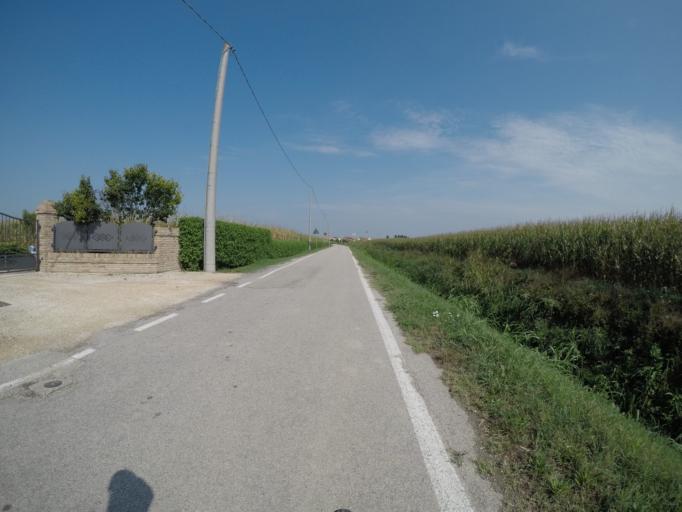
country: IT
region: Veneto
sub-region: Provincia di Rovigo
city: Lendinara
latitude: 45.0981
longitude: 11.5893
